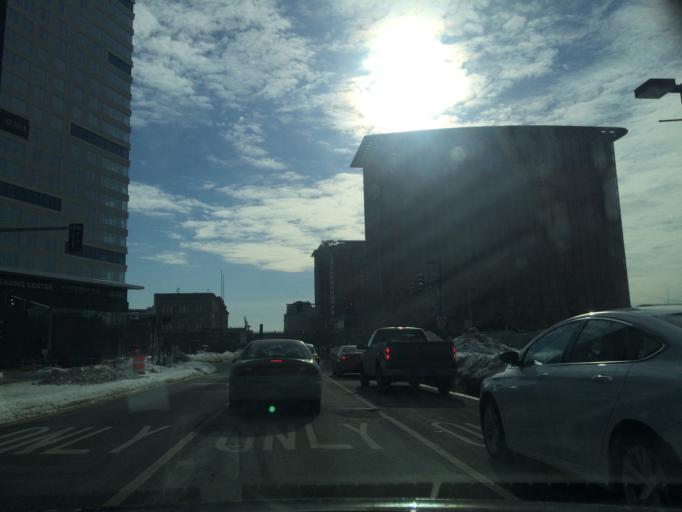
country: US
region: Massachusetts
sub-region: Suffolk County
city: Boston
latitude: 42.3513
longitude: -71.0446
